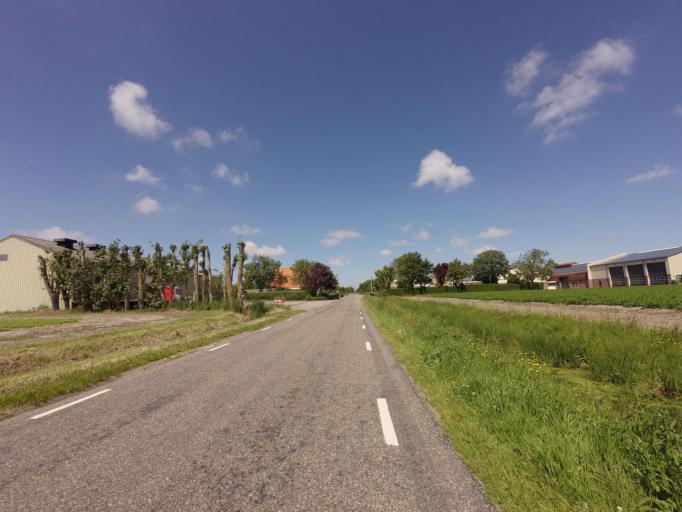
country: NL
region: North Holland
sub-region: Gemeente Schagen
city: Schagen
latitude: 52.8849
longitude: 4.8297
